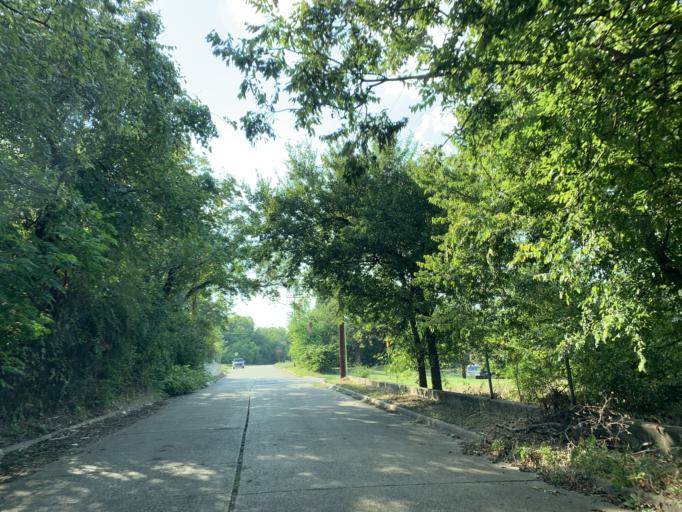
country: US
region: Texas
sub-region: Dallas County
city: Dallas
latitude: 32.7513
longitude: -96.8019
